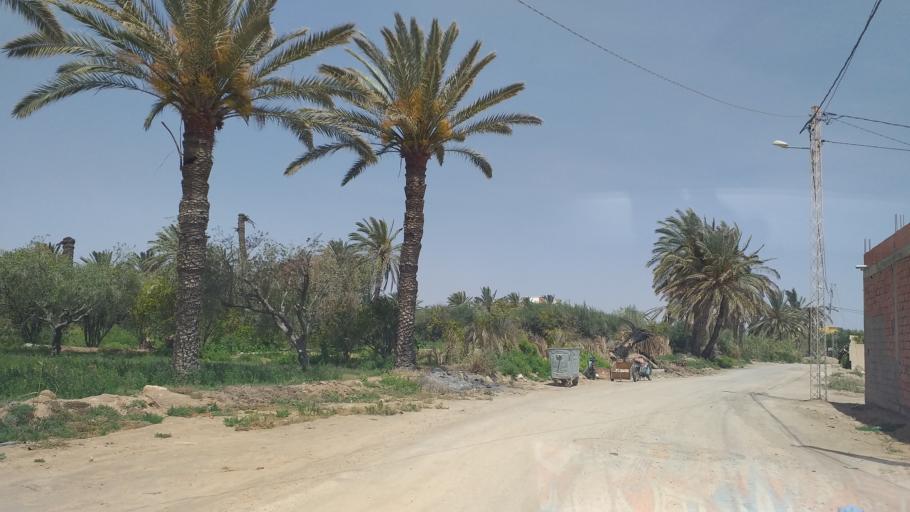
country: TN
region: Qabis
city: Gabes
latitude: 33.9474
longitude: 10.0638
